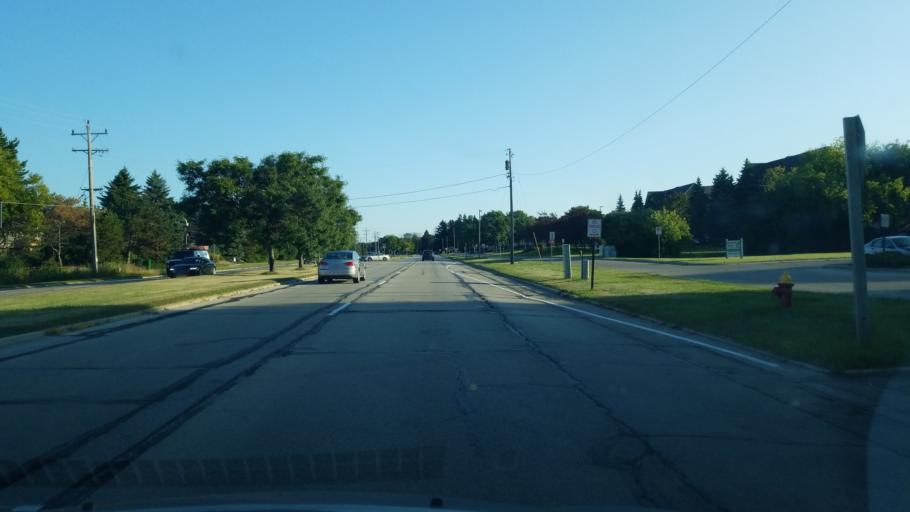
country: US
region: Wisconsin
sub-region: Milwaukee County
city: Brown Deer
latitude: 43.1875
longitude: -87.9643
